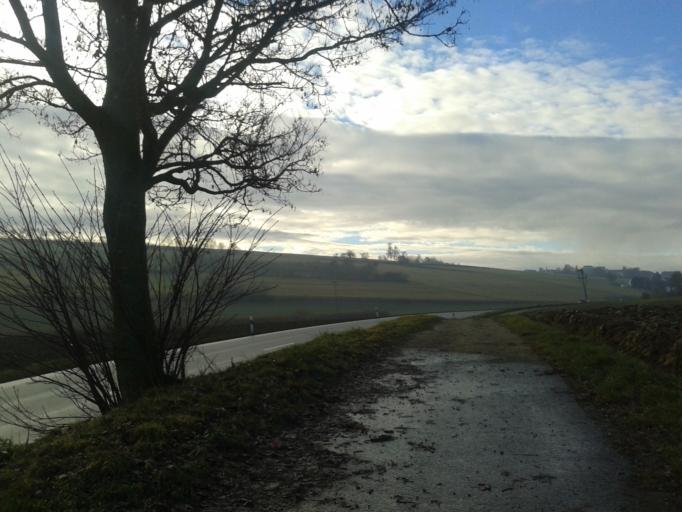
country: DE
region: Baden-Wuerttemberg
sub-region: Tuebingen Region
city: Erbach
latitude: 48.3843
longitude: 9.9064
